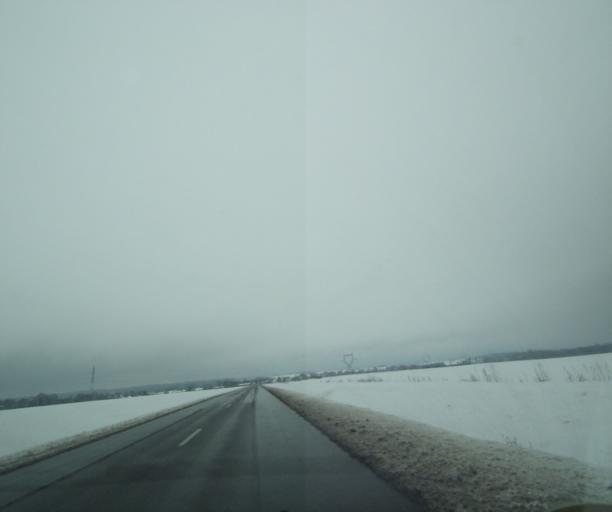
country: FR
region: Champagne-Ardenne
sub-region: Departement de la Haute-Marne
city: Montier-en-Der
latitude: 48.4974
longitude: 4.7840
